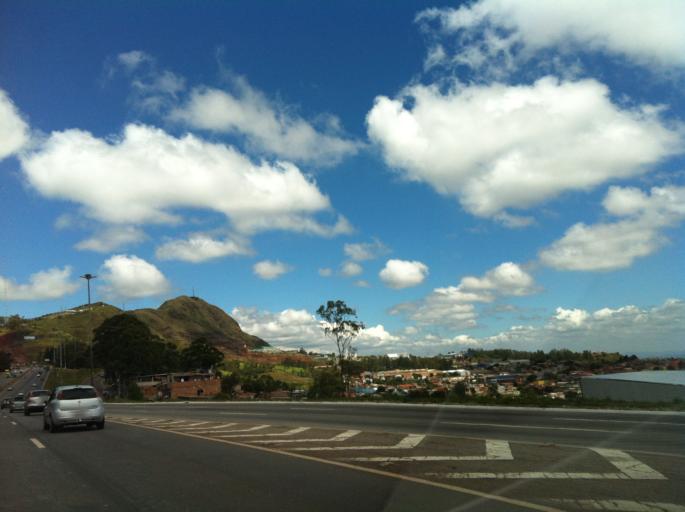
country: BR
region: Minas Gerais
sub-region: Belo Horizonte
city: Belo Horizonte
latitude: -19.9963
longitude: -43.9613
